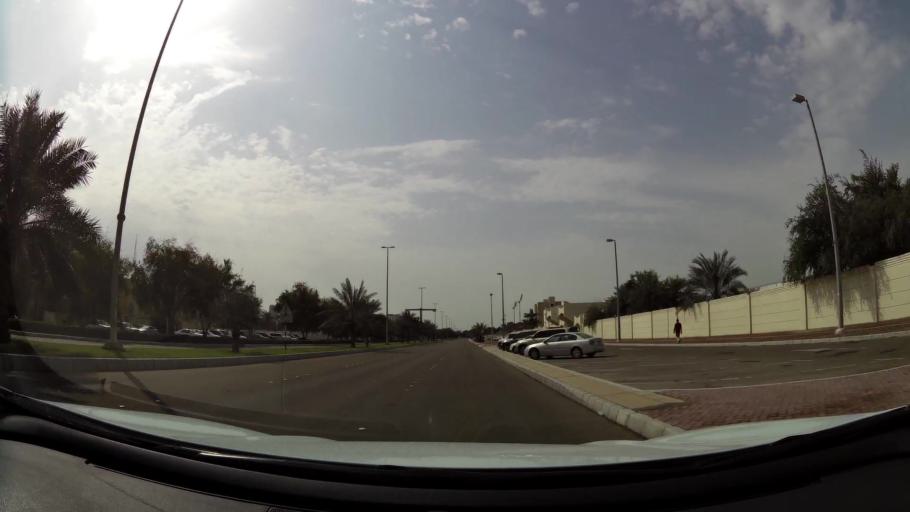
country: AE
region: Abu Dhabi
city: Abu Dhabi
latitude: 24.4410
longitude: 54.4277
